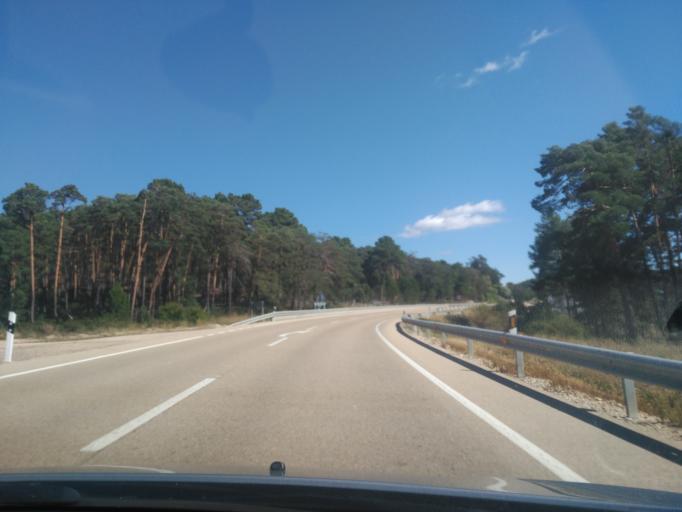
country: ES
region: Castille and Leon
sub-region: Provincia de Soria
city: Navaleno
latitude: 41.8394
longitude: -3.0185
